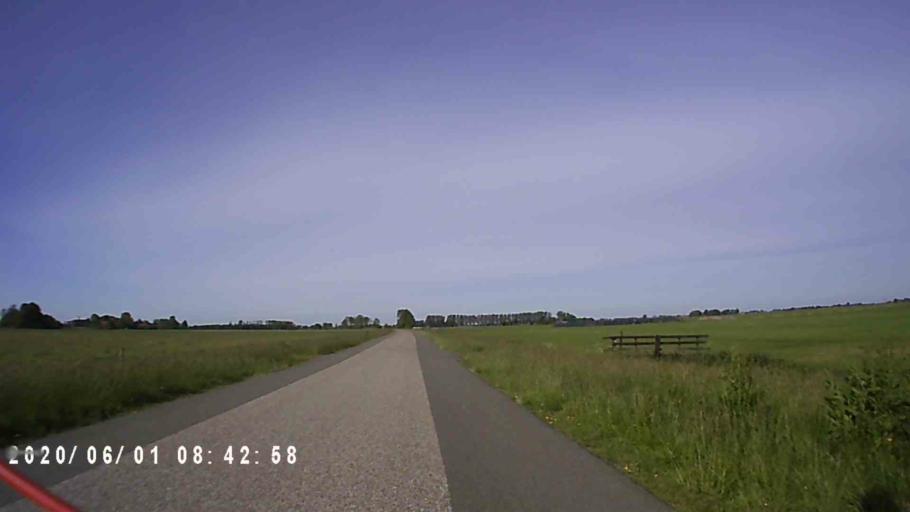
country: NL
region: Friesland
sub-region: Gemeente Ferwerderadiel
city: Burdaard
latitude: 53.2847
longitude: 5.8443
